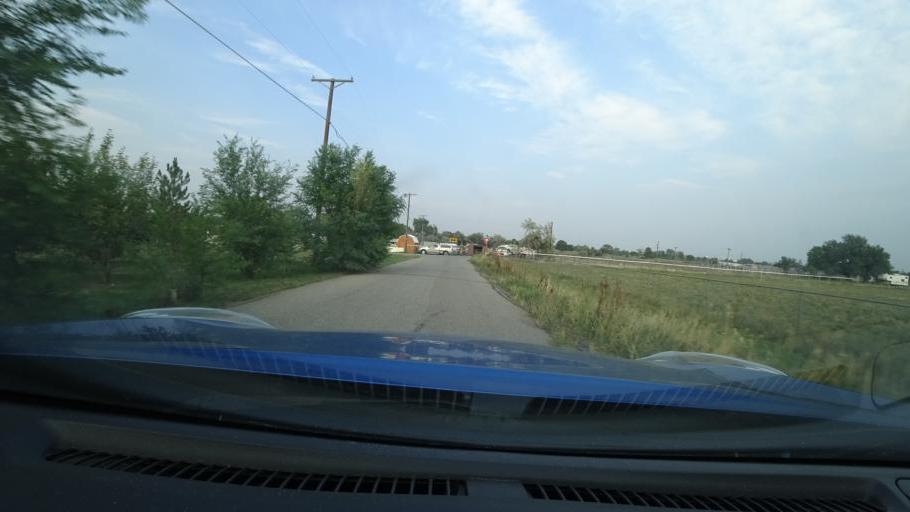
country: US
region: Colorado
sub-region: Adams County
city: Aurora
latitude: 39.7364
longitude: -104.7850
